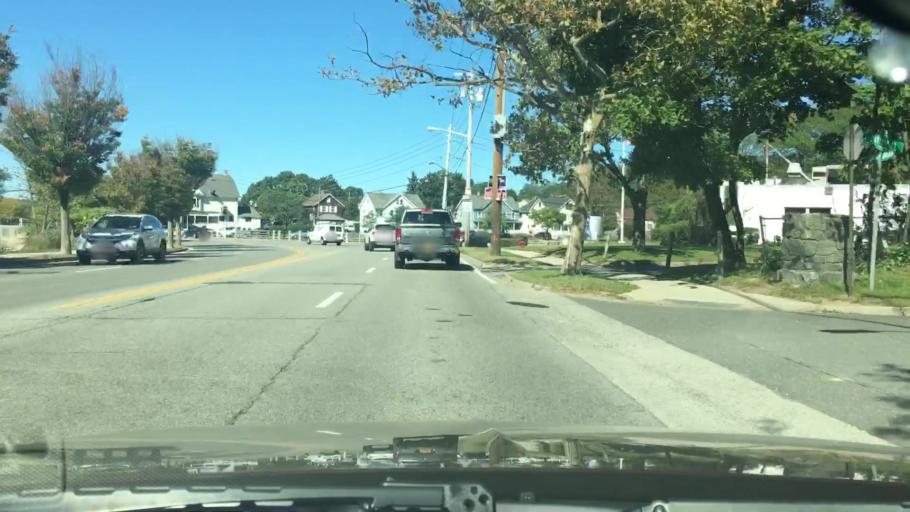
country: US
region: New York
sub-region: Nassau County
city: Port Washington
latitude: 40.8348
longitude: -73.6998
